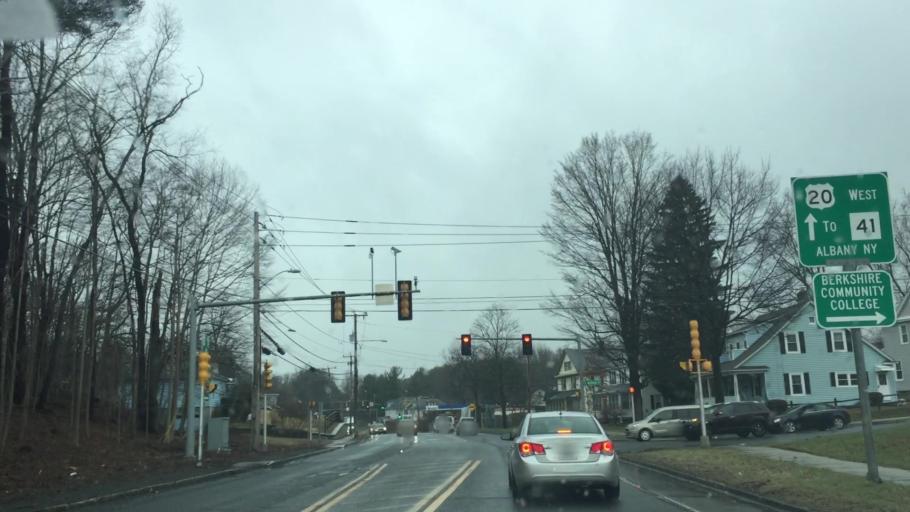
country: US
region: Massachusetts
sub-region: Berkshire County
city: Pittsfield
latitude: 42.4430
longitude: -73.2676
